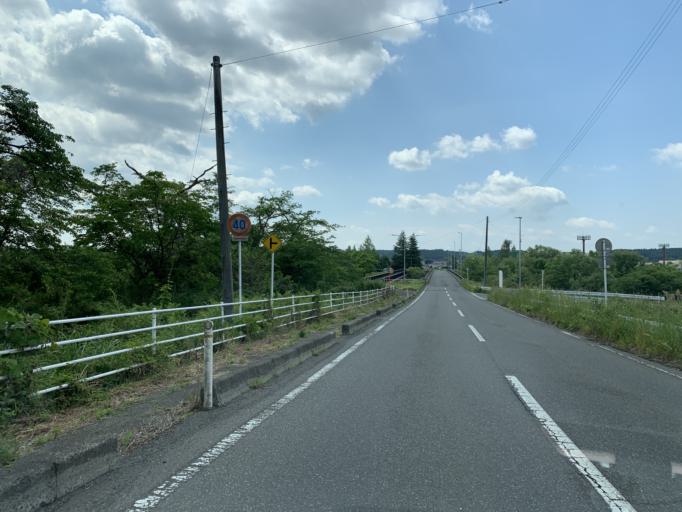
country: JP
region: Miyagi
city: Furukawa
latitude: 38.7477
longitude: 140.9536
